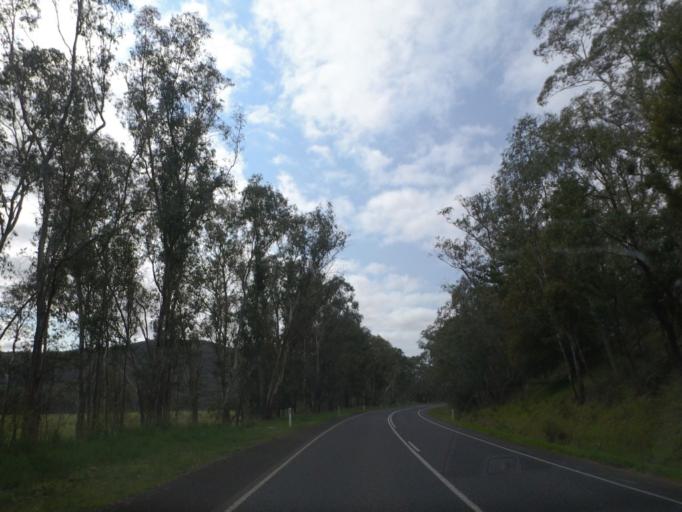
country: AU
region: Victoria
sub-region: Murrindindi
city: Kinglake West
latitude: -37.1408
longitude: 145.2598
